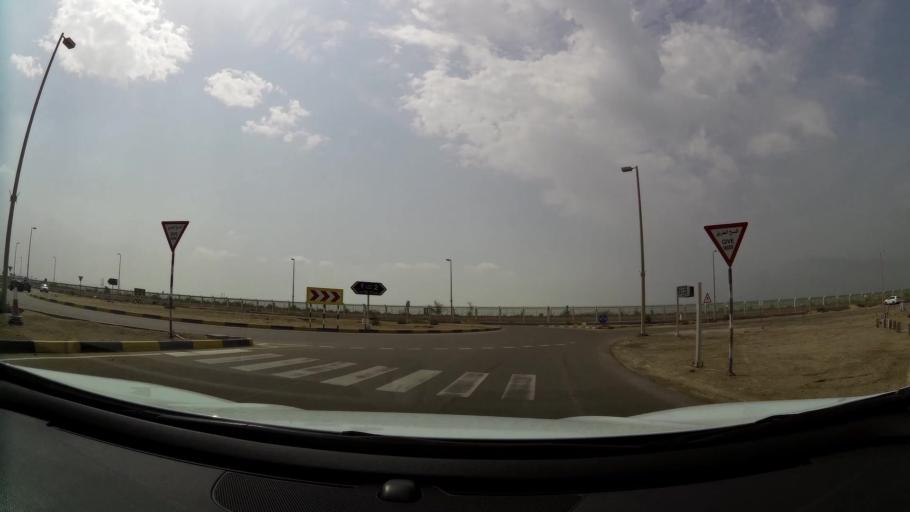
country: AE
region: Abu Dhabi
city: Abu Dhabi
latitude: 24.5355
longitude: 54.6328
